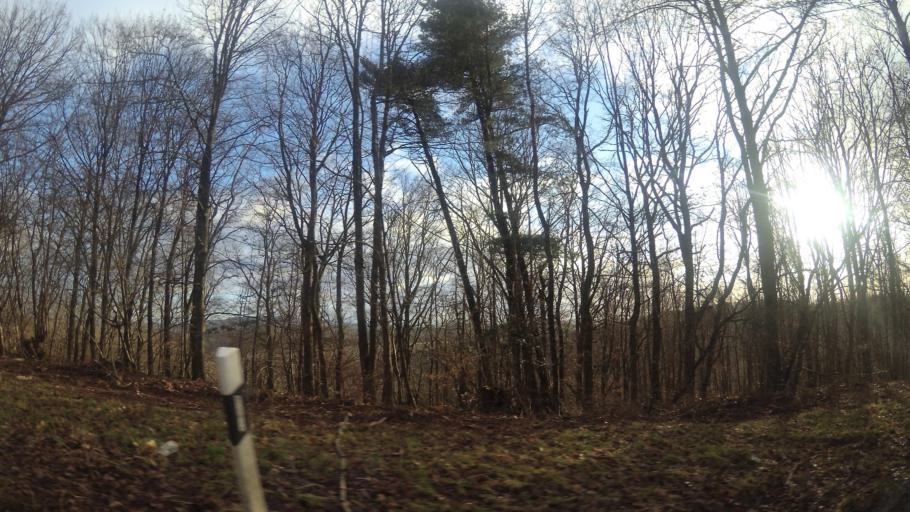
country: DE
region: Rheinland-Pfalz
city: Oberalben
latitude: 49.5776
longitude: 7.4229
